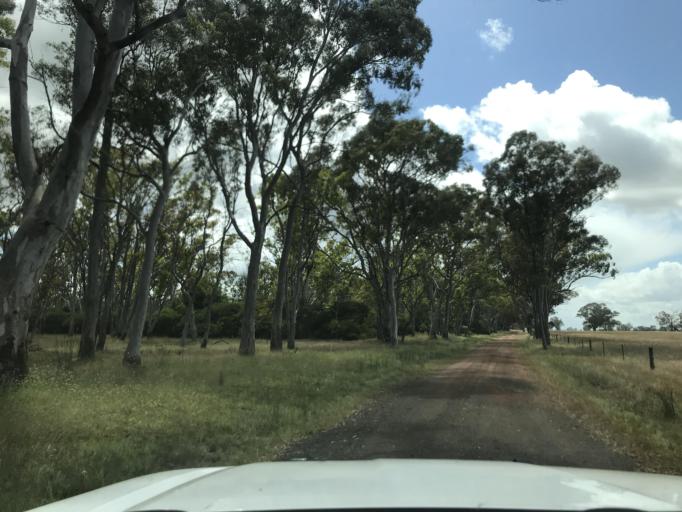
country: AU
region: South Australia
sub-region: Wattle Range
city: Penola
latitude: -37.1814
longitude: 141.4425
